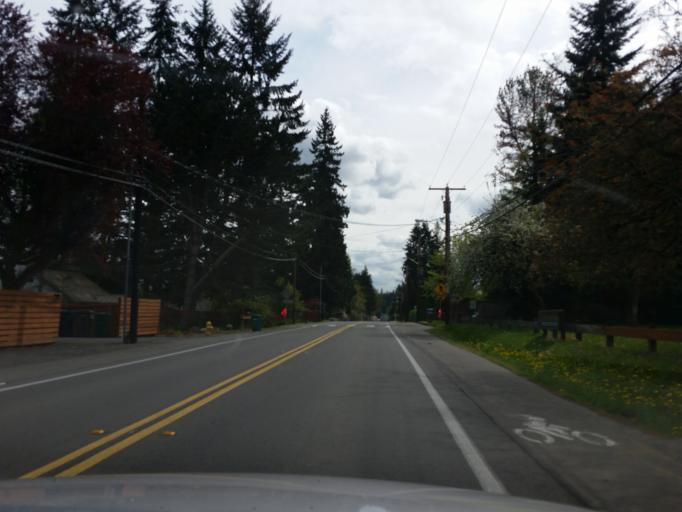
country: US
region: Washington
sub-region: King County
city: Kingsgate
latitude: 47.6961
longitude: -122.1647
